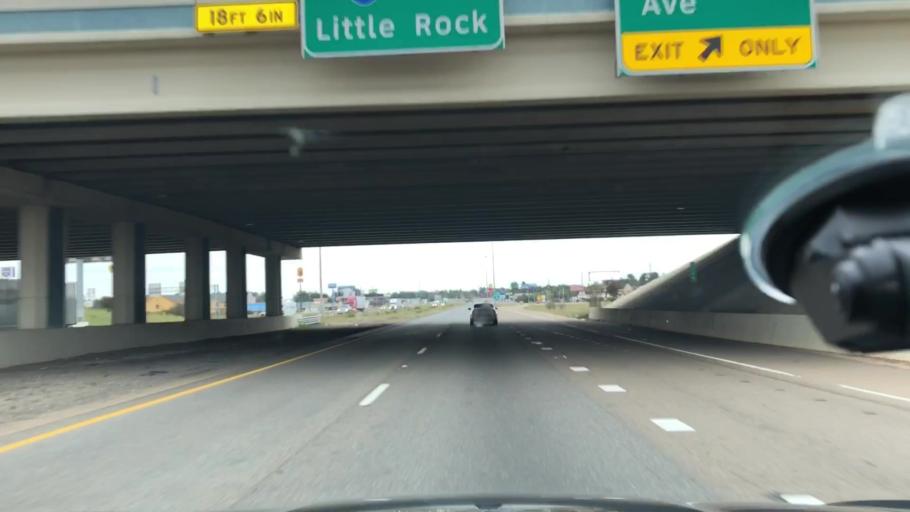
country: US
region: Arkansas
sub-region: Miller County
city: Texarkana
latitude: 33.4701
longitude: -94.0437
